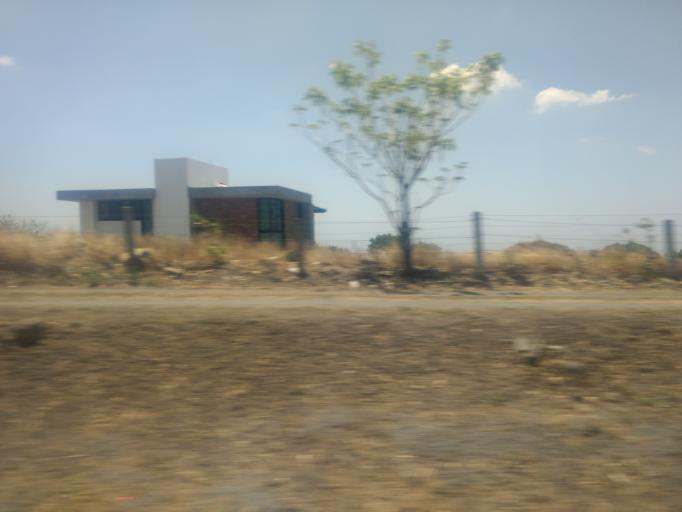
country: MX
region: Colima
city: Queseria
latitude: 19.3690
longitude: -103.5615
